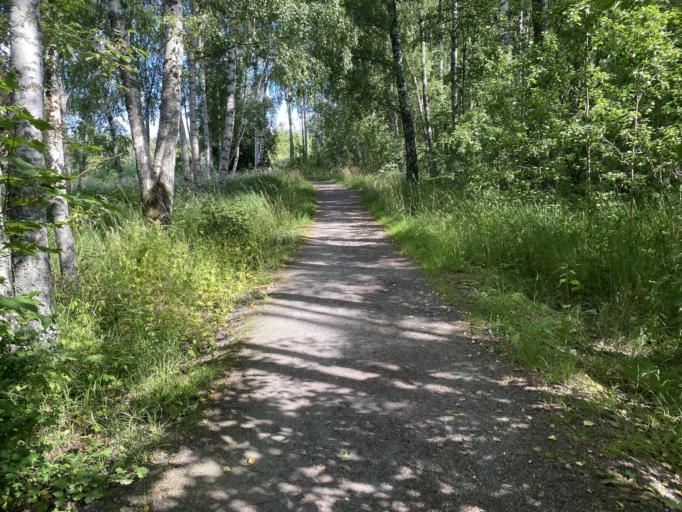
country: SE
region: Stockholm
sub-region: Upplands Vasby Kommun
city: Upplands Vaesby
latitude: 59.4865
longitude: 17.8985
